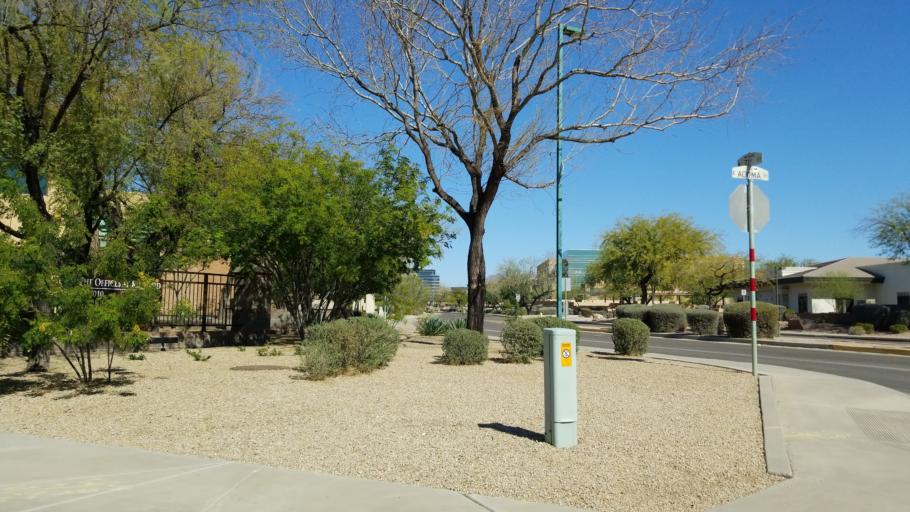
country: US
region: Arizona
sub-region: Maricopa County
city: Paradise Valley
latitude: 33.6187
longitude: -111.9297
